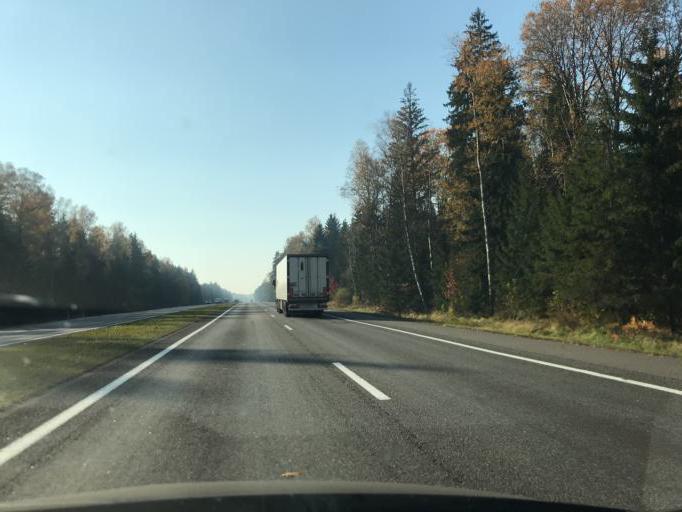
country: BY
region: Minsk
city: Stowbtsy
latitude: 53.5356
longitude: 26.8885
